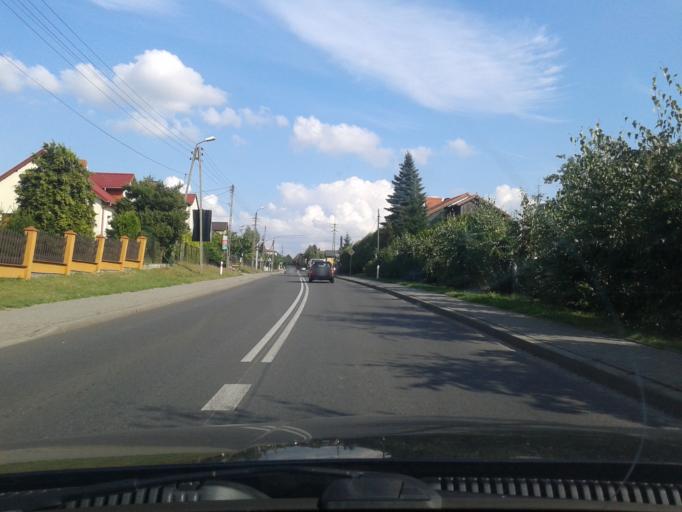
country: PL
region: Silesian Voivodeship
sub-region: Powiat wodzislawski
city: Gorzyce
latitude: 49.9599
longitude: 18.3924
